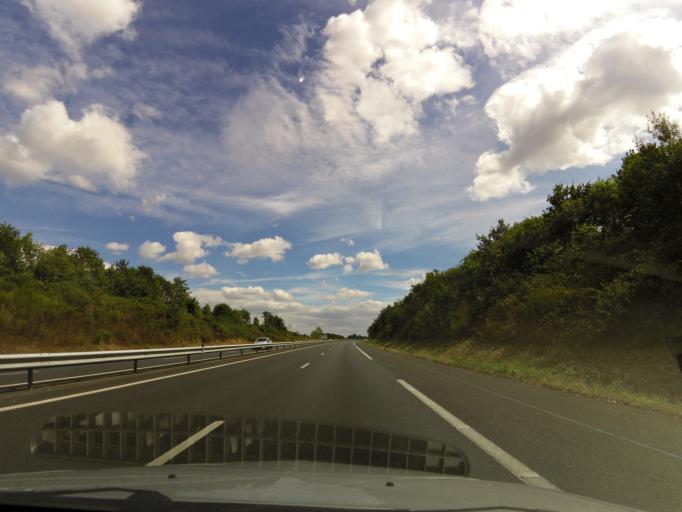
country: FR
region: Pays de la Loire
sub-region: Departement de la Vendee
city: Les Brouzils
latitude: 46.9023
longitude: -1.3093
